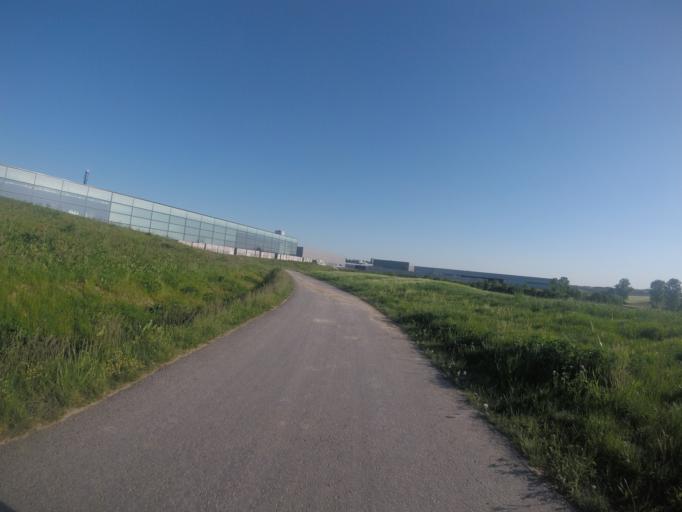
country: DE
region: Baden-Wuerttemberg
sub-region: Regierungsbezirk Stuttgart
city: Backnang
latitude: 48.9671
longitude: 9.4240
